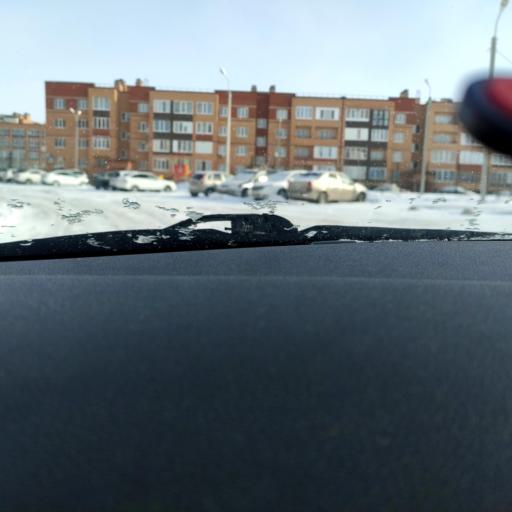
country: RU
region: Bashkortostan
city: Ufa
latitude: 54.6209
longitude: 55.8814
